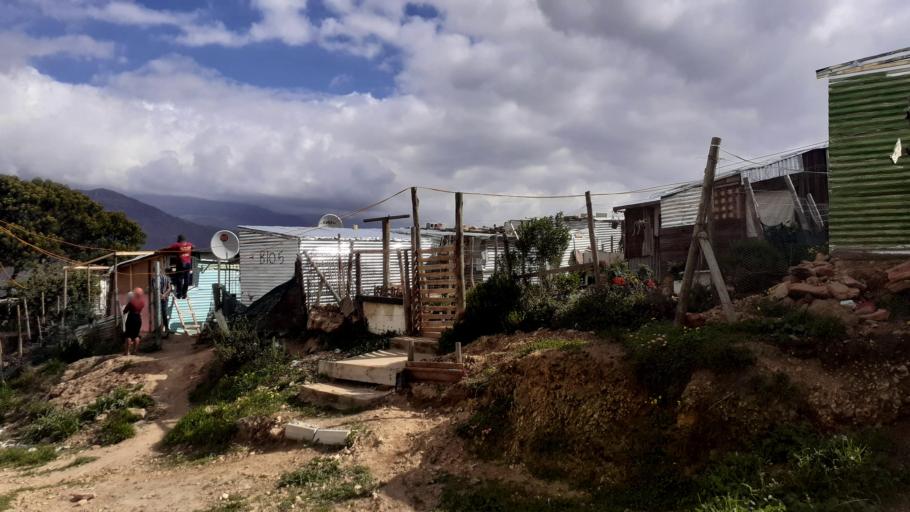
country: ZA
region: Western Cape
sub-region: Cape Winelands District Municipality
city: Paarl
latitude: -33.8858
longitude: 19.1077
